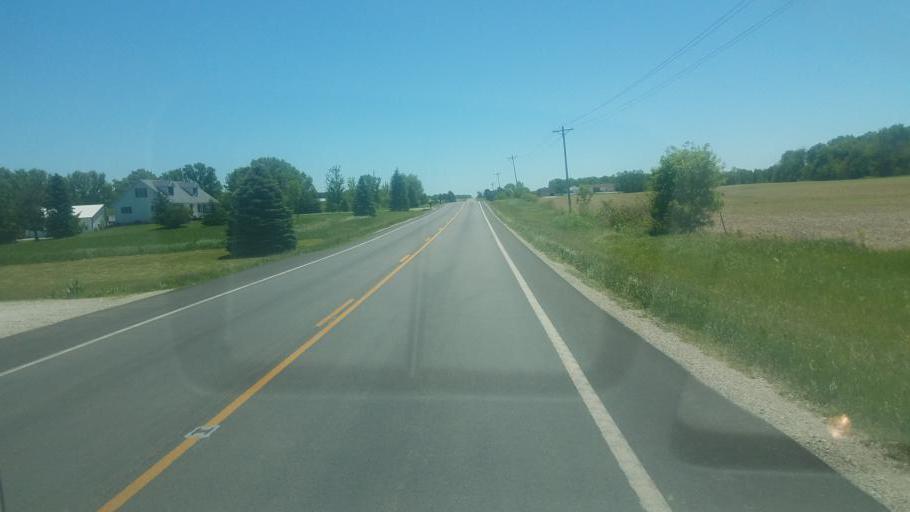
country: US
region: Ohio
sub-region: Miami County
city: Covington
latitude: 40.2308
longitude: -84.3569
